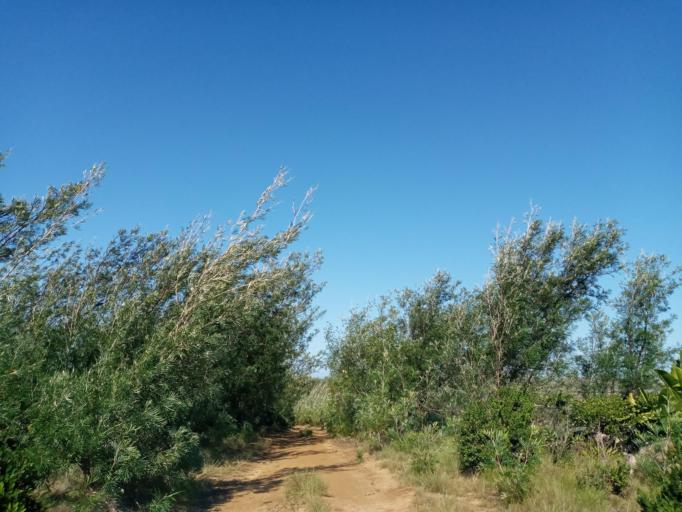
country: MG
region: Anosy
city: Fort Dauphin
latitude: -24.9134
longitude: 47.0835
